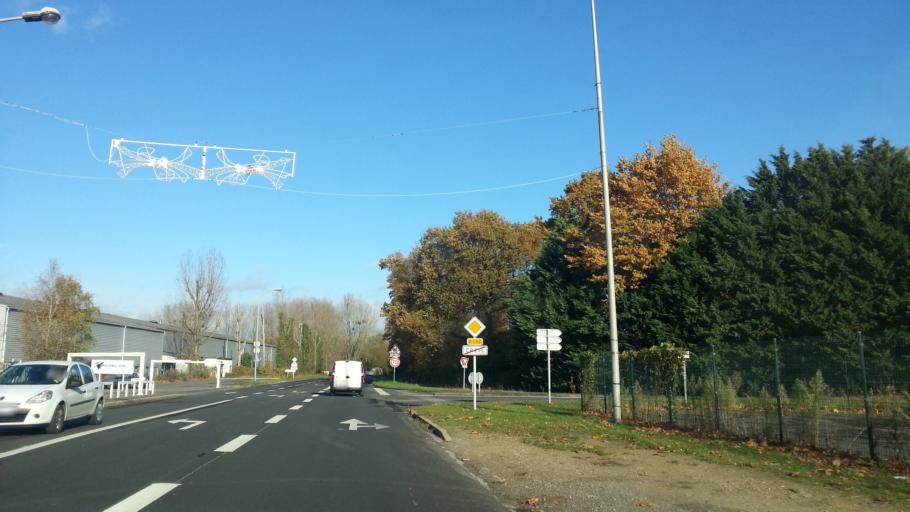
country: FR
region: Picardie
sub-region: Departement de l'Oise
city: Villers-Saint-Paul
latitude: 49.2731
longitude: 2.4972
